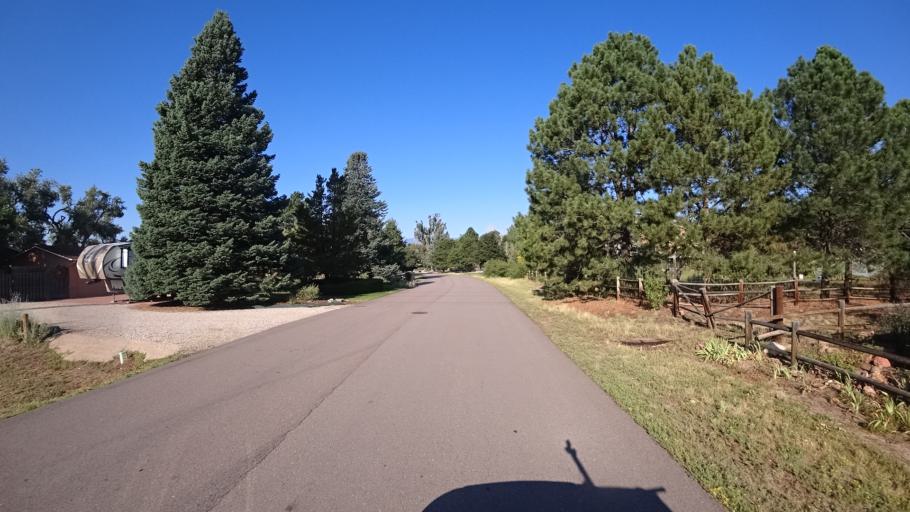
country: US
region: Colorado
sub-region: El Paso County
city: Air Force Academy
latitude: 38.9312
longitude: -104.7844
